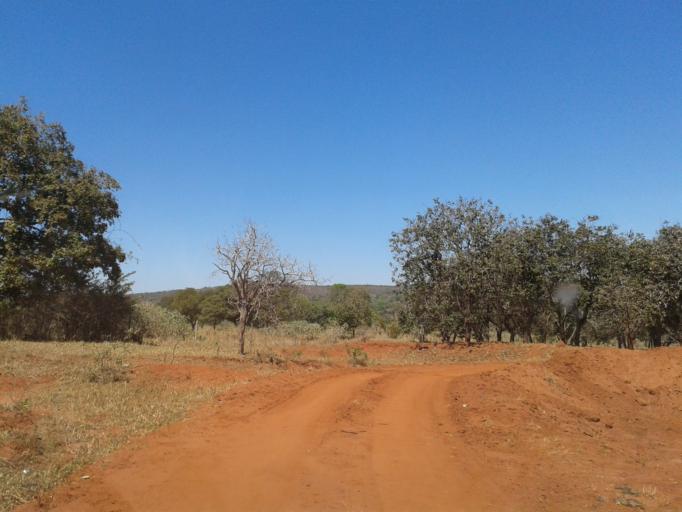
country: BR
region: Minas Gerais
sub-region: Ituiutaba
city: Ituiutaba
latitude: -19.1094
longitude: -49.2714
